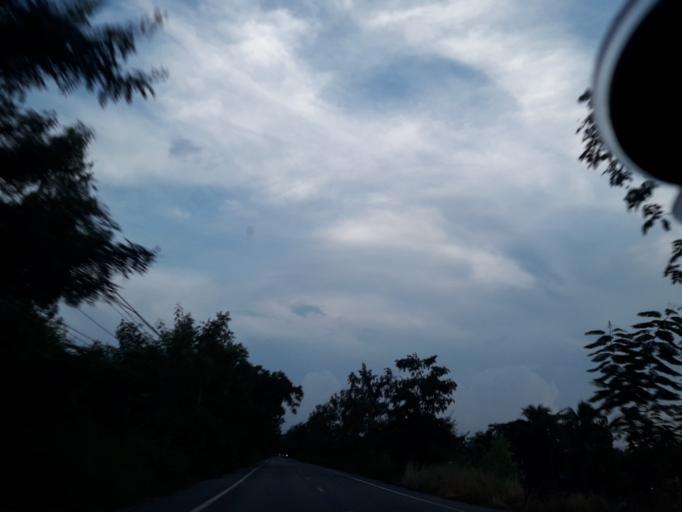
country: TH
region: Pathum Thani
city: Nong Suea
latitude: 14.1560
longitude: 100.8690
